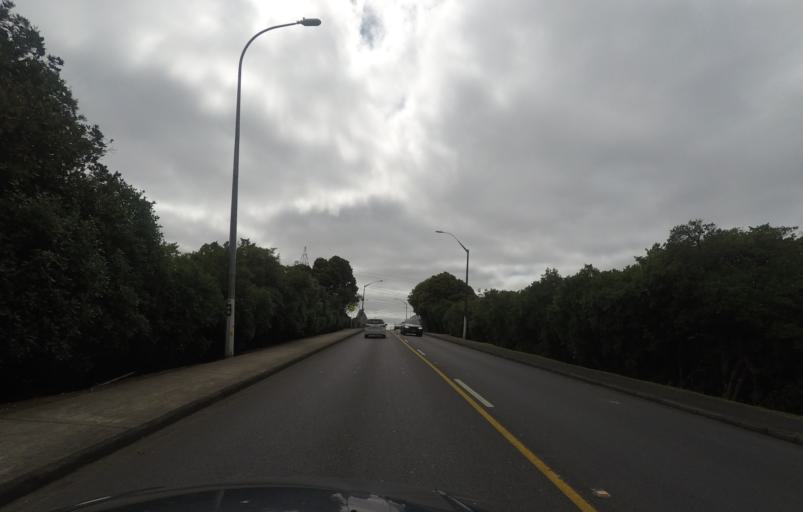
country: NZ
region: Auckland
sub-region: Auckland
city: Manukau City
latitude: -36.9575
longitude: 174.8607
